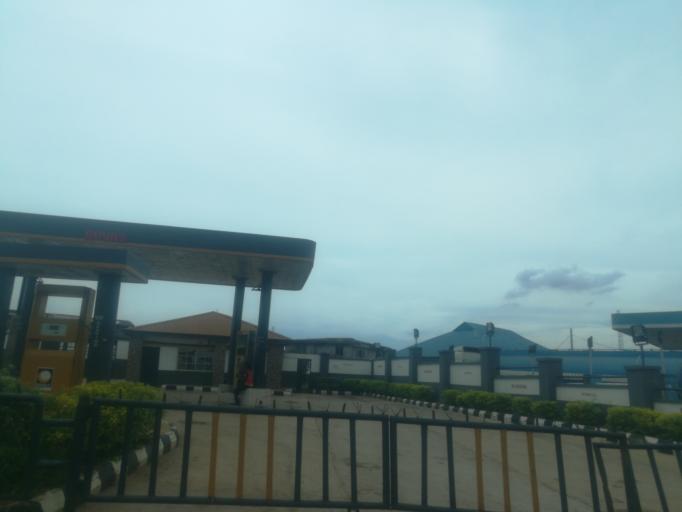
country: NG
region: Oyo
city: Ibadan
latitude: 7.3785
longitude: 3.9392
